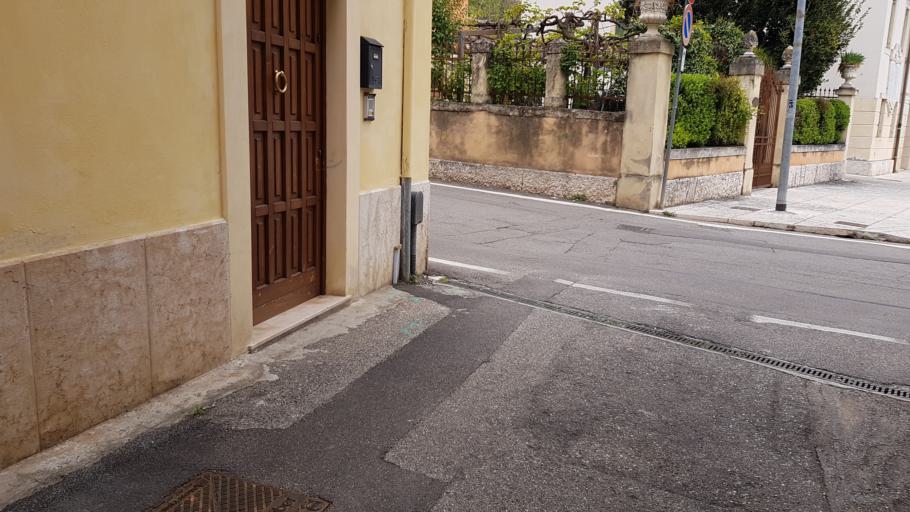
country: IT
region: Veneto
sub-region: Provincia di Verona
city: Parona
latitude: 45.4720
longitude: 10.9744
